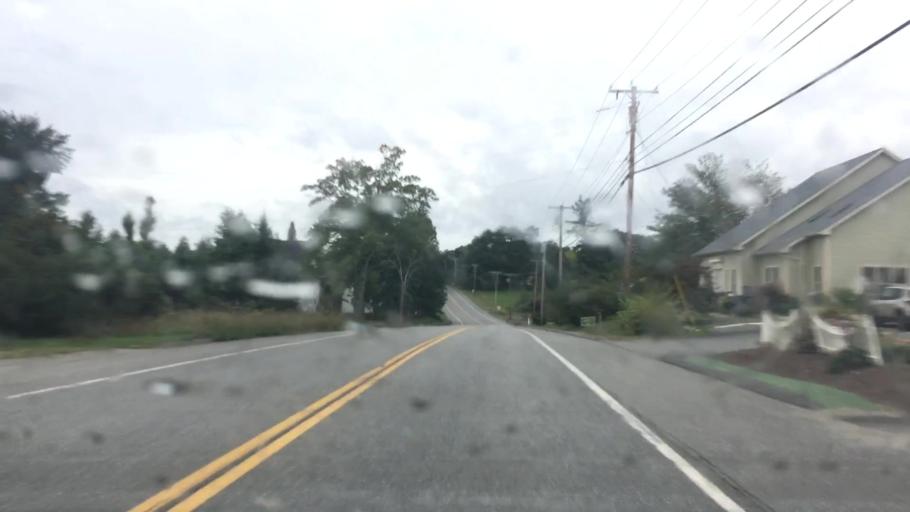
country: US
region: Maine
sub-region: Penobscot County
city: Orrington
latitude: 44.7192
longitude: -68.8265
